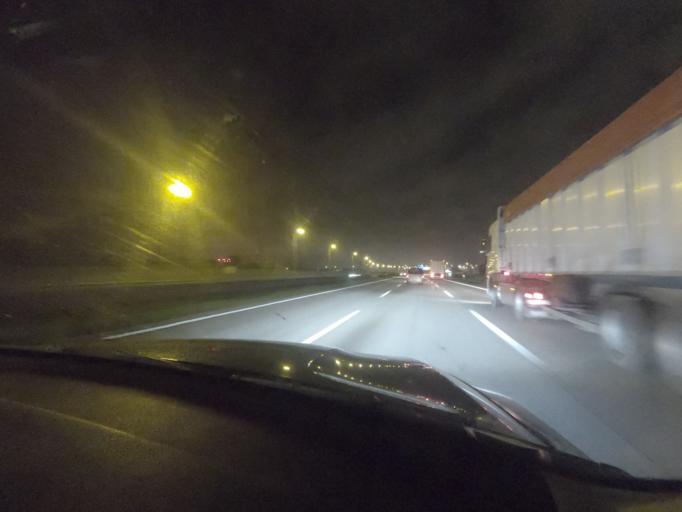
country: PT
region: Lisbon
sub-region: Alenquer
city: Carregado
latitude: 39.0313
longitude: -8.9610
